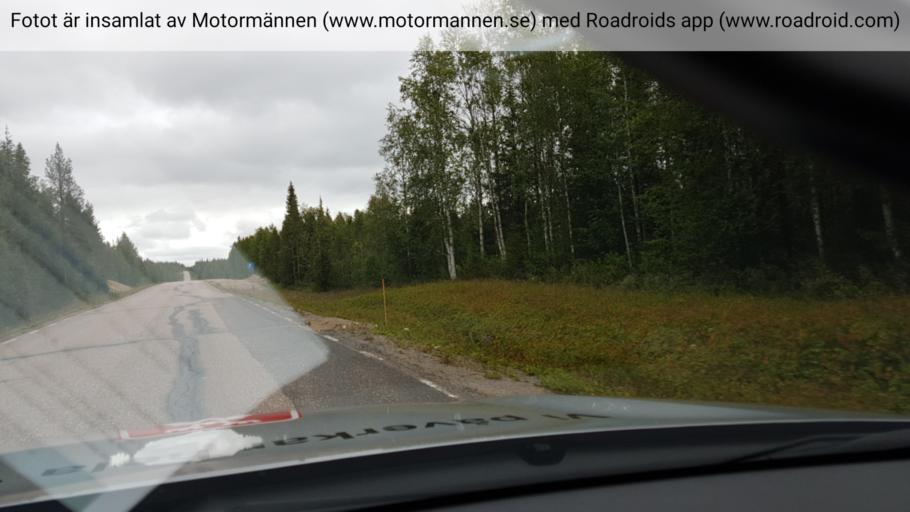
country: SE
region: Norrbotten
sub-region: Overkalix Kommun
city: OEverkalix
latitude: 67.0342
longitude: 22.0223
